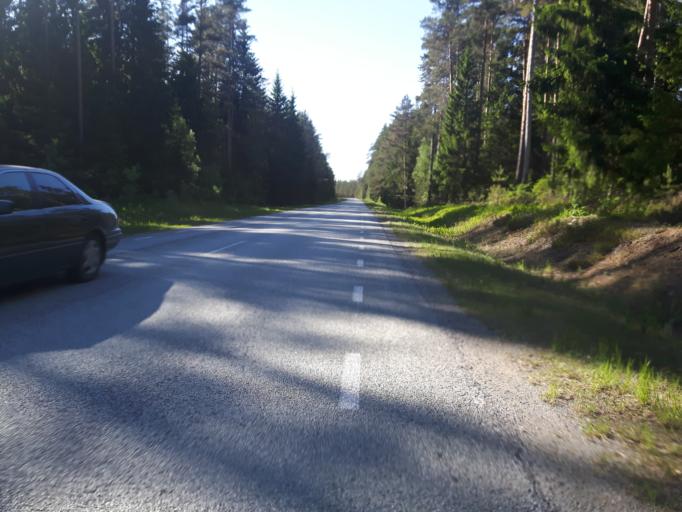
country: EE
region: Laeaene-Virumaa
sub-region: Kadrina vald
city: Kadrina
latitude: 59.5497
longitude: 26.0159
